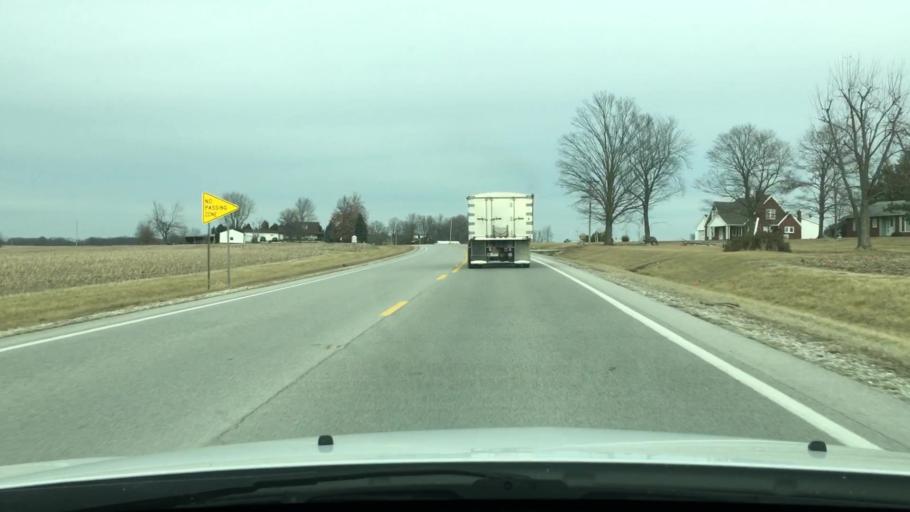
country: US
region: Illinois
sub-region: Pike County
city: Pittsfield
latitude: 39.6445
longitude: -90.7849
